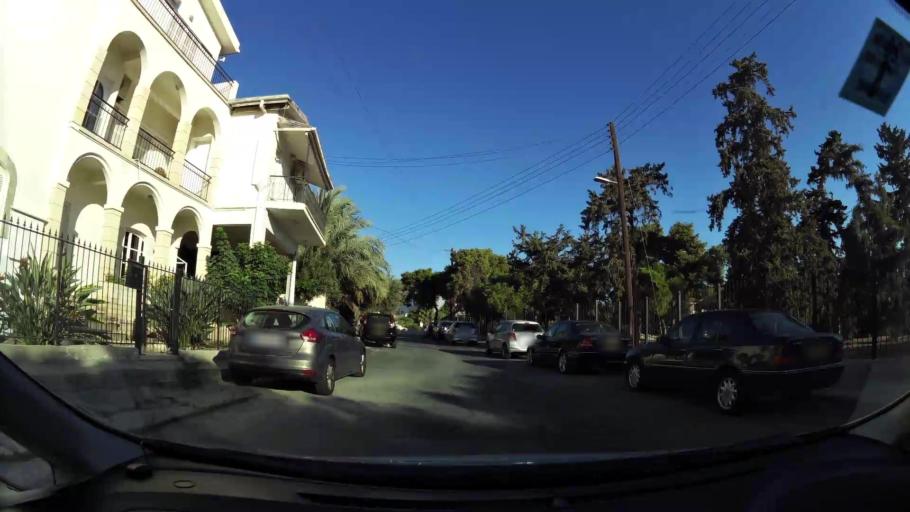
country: CY
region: Larnaka
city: Larnaca
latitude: 34.9202
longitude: 33.6323
